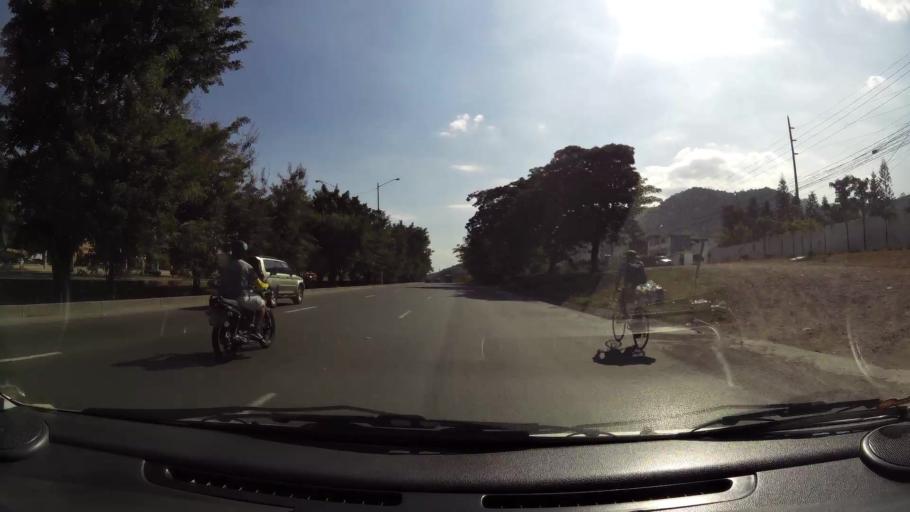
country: EC
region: Guayas
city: Santa Lucia
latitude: -2.1824
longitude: -79.9907
